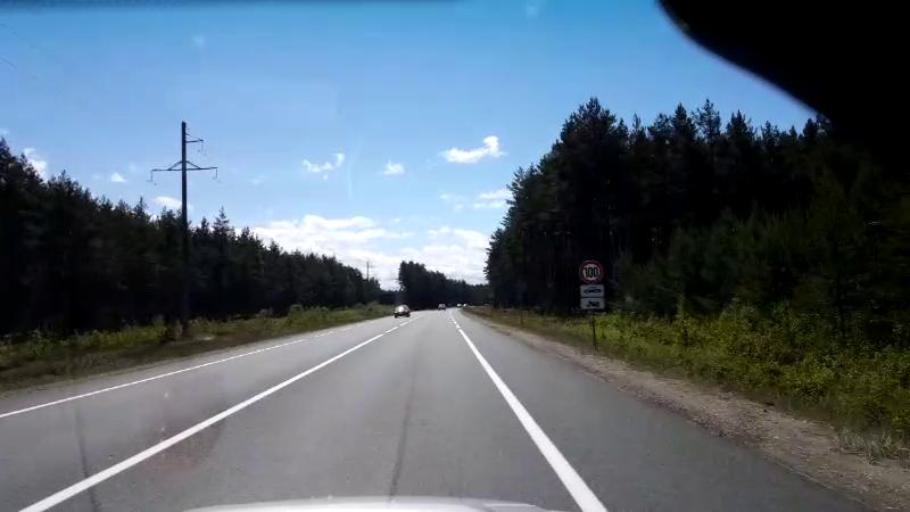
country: LV
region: Saulkrastu
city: Saulkrasti
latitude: 57.2374
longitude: 24.4272
